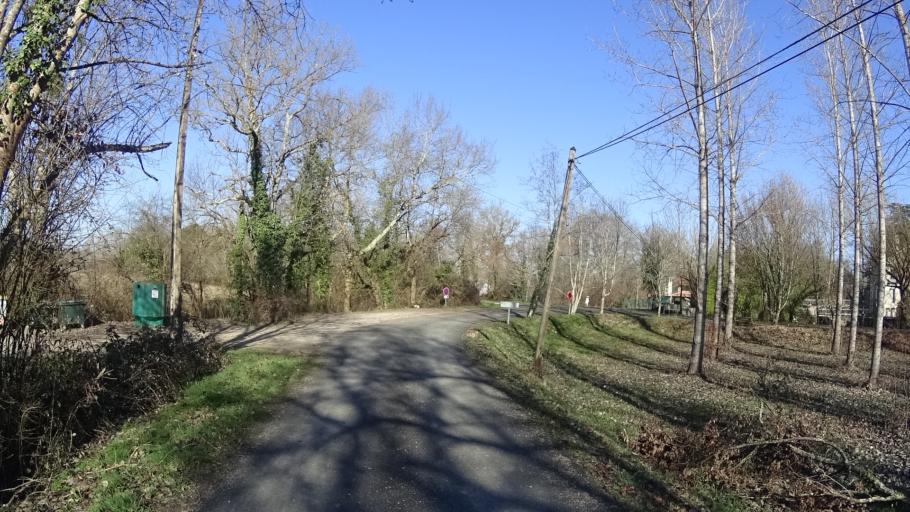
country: FR
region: Aquitaine
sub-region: Departement de la Dordogne
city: Montpon-Menesterol
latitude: 45.0287
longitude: 0.2253
